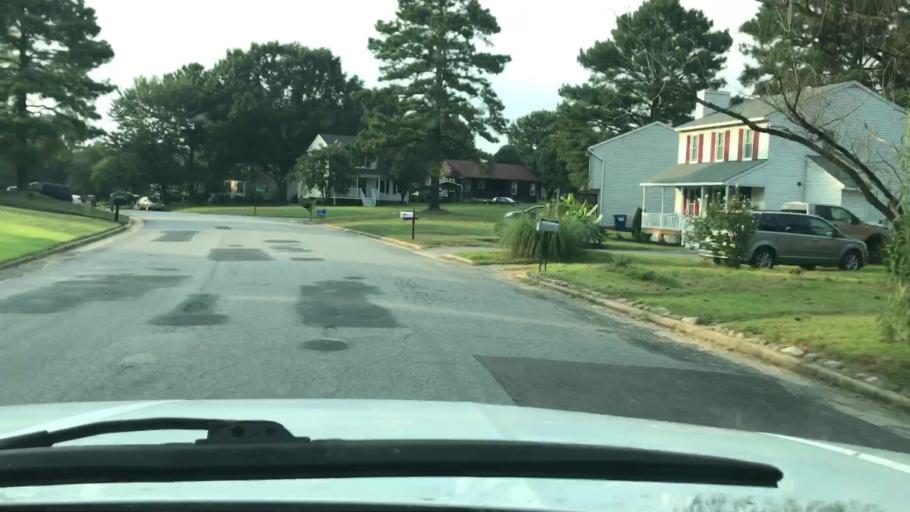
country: US
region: Virginia
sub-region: Chesterfield County
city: Chesterfield
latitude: 37.4400
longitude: -77.5170
